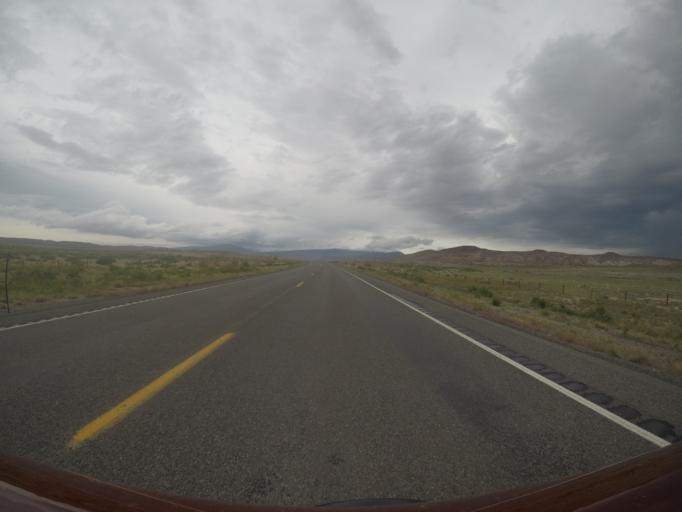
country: US
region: Wyoming
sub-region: Big Horn County
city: Lovell
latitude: 44.9127
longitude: -108.2920
